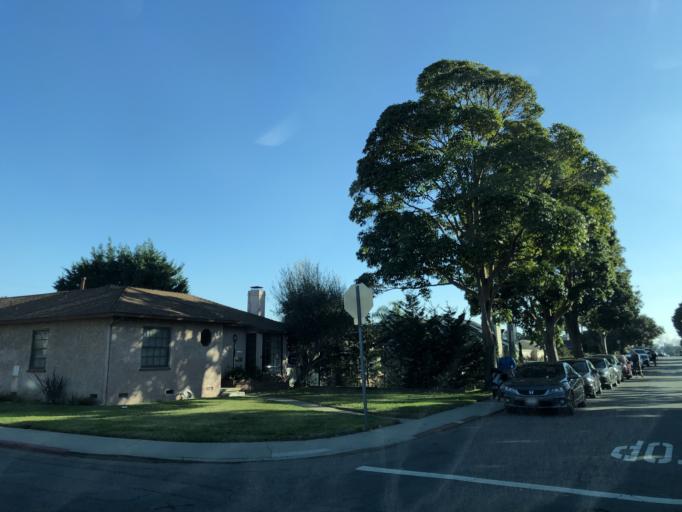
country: US
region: California
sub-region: Los Angeles County
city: El Segundo
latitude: 33.9222
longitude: -118.4147
